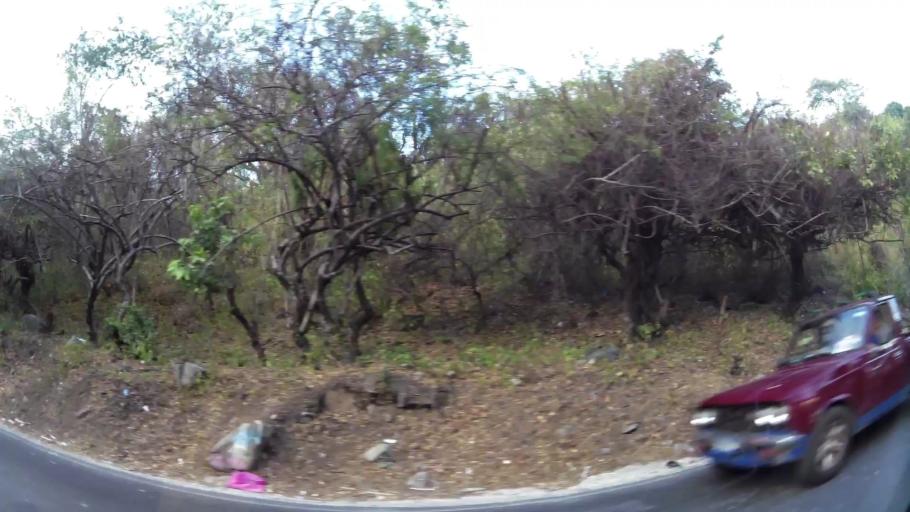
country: SV
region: San Vicente
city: Apastepeque
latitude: 13.6517
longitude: -88.7862
